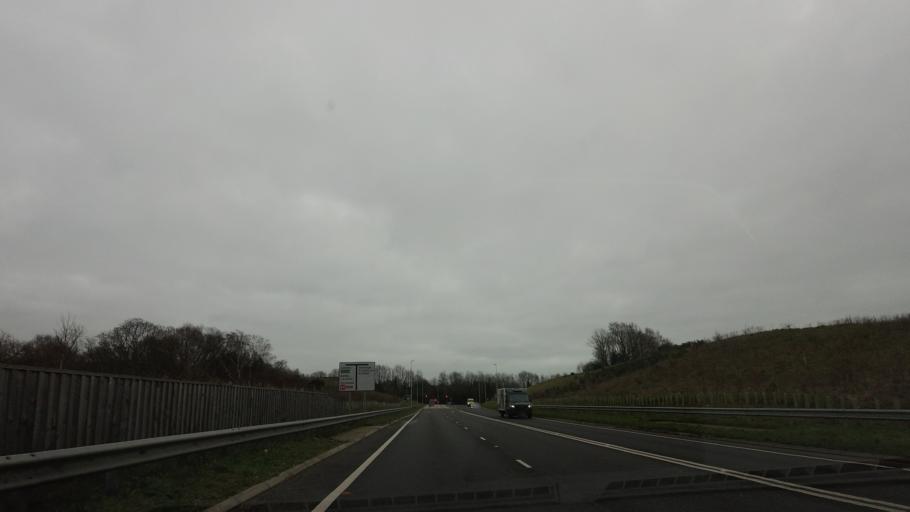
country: GB
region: England
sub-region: East Sussex
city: Saint Leonards-on-Sea
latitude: 50.8721
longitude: 0.5204
